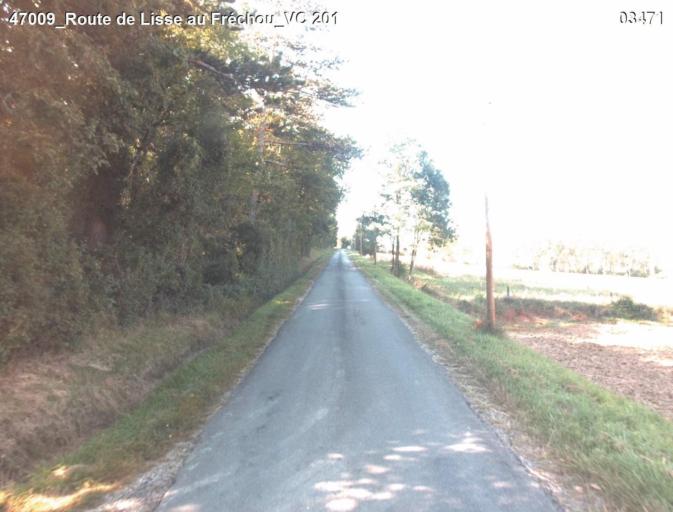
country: FR
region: Aquitaine
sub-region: Departement du Lot-et-Garonne
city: Mezin
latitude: 44.1002
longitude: 0.2759
